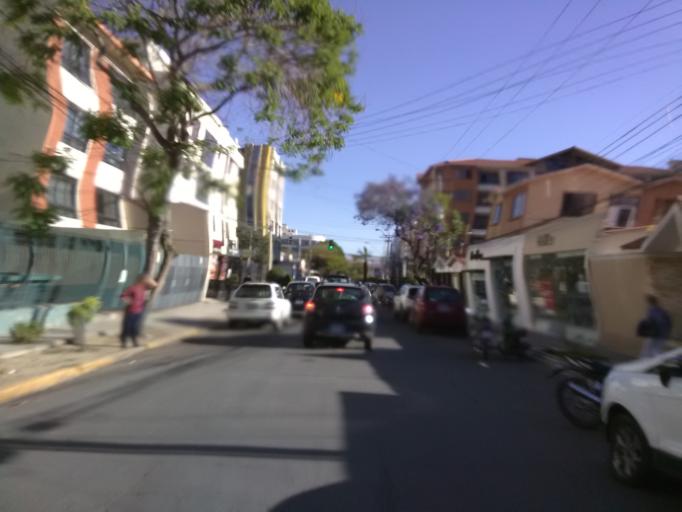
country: BO
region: Cochabamba
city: Cochabamba
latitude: -17.3767
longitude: -66.1540
